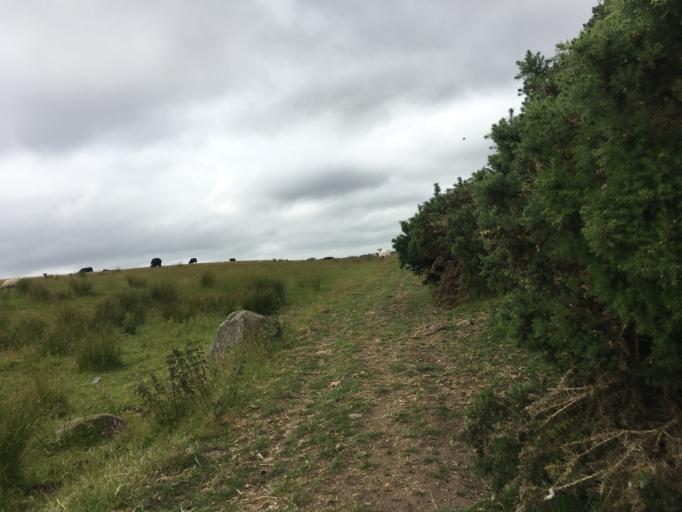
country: GB
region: England
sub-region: Northumberland
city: Belford
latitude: 55.6140
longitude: -1.8934
